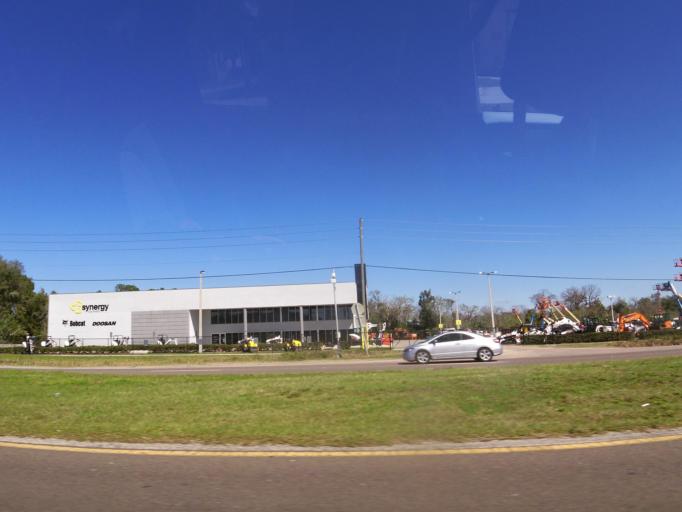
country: US
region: Florida
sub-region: Orange County
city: Lockhart
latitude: 28.6315
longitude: -81.4510
